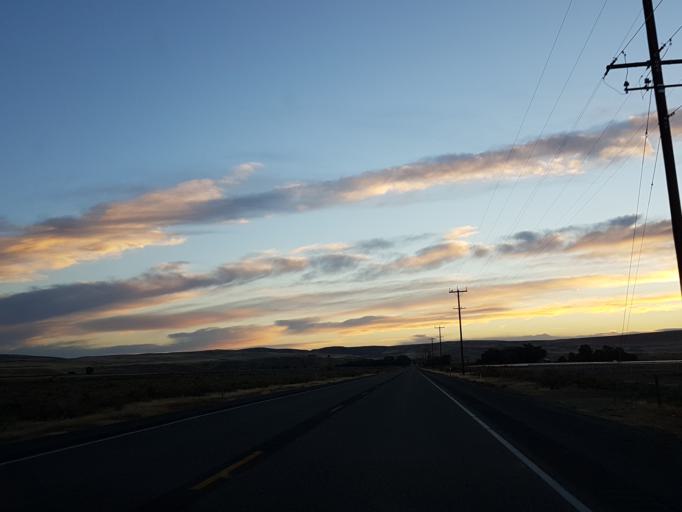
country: US
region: Oregon
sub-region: Malheur County
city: Vale
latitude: 43.9369
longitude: -117.3772
